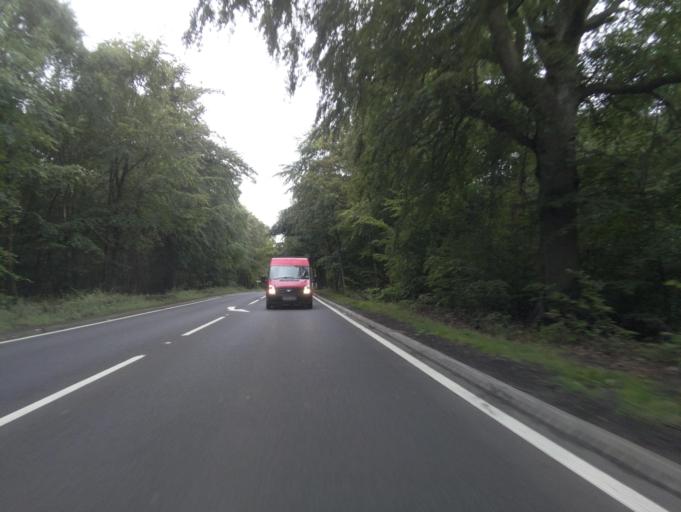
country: GB
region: Scotland
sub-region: Fife
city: High Valleyfield
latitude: 56.0659
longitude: -3.6550
